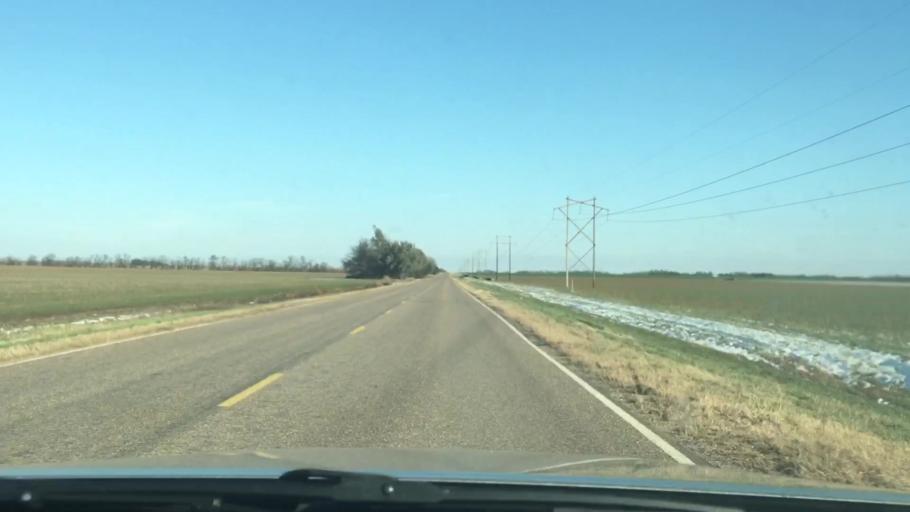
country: US
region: Kansas
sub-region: Rice County
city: Lyons
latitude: 38.2895
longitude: -98.1180
